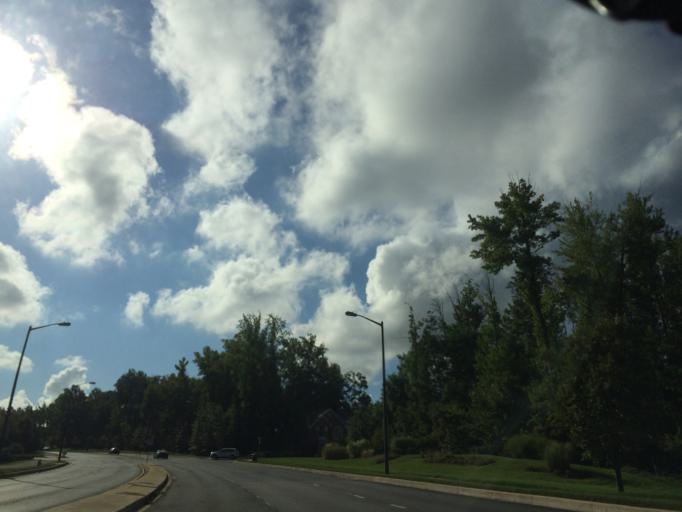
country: US
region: Maryland
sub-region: Anne Arundel County
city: Jessup
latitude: 39.1511
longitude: -76.7405
